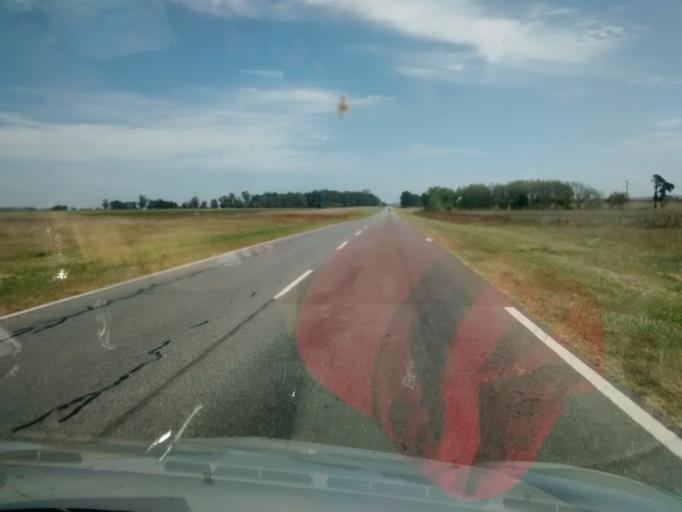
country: AR
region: Buenos Aires
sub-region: Partido de Balcarce
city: Balcarce
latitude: -37.6696
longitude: -58.5244
